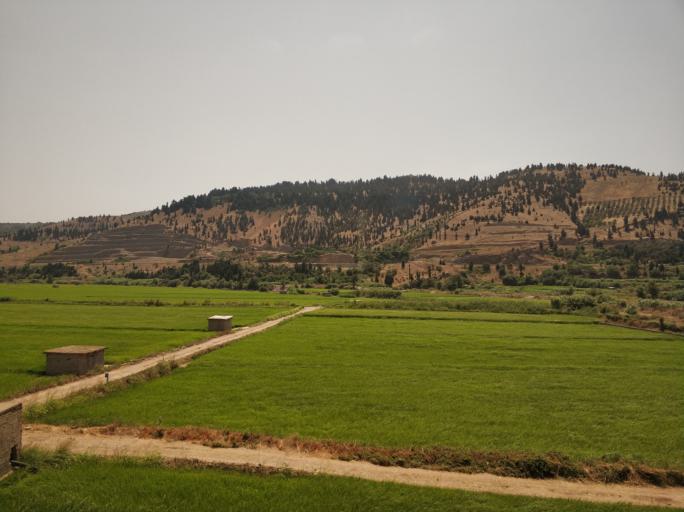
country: IR
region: Gilan
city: Pa'in-e Bazar-e Rudbar
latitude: 36.8662
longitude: 49.4890
